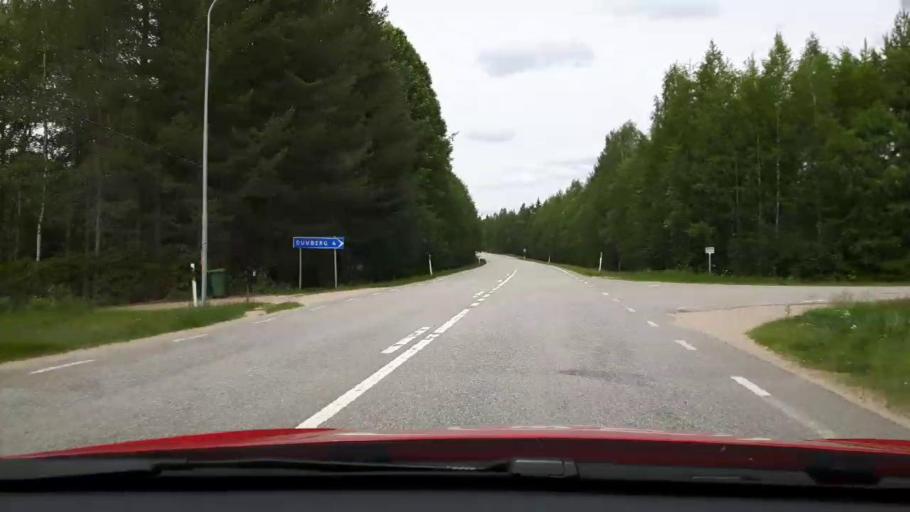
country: SE
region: Jaemtland
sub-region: Harjedalens Kommun
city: Sveg
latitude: 62.0721
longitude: 14.2707
